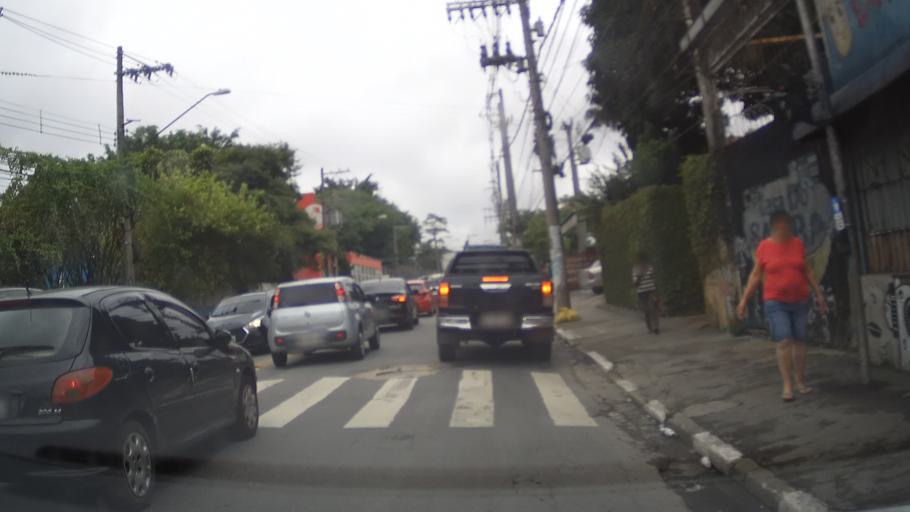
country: BR
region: Sao Paulo
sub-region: Guarulhos
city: Guarulhos
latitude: -23.4315
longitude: -46.5031
